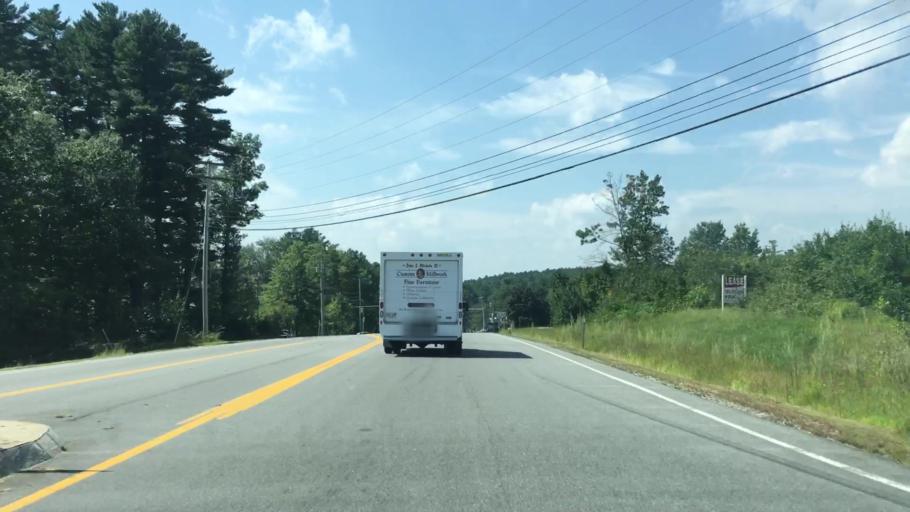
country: US
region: New Hampshire
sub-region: Rockingham County
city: Windham
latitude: 42.8061
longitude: -71.2913
